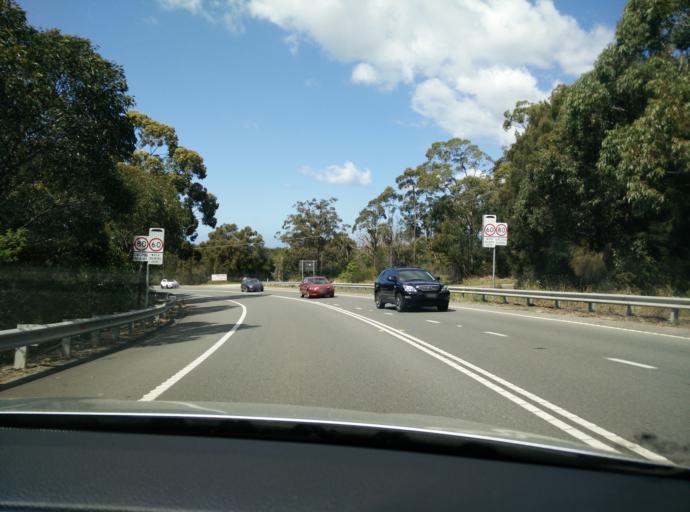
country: AU
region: New South Wales
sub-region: Gosford Shire
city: Blackwall
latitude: -33.4785
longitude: 151.2915
